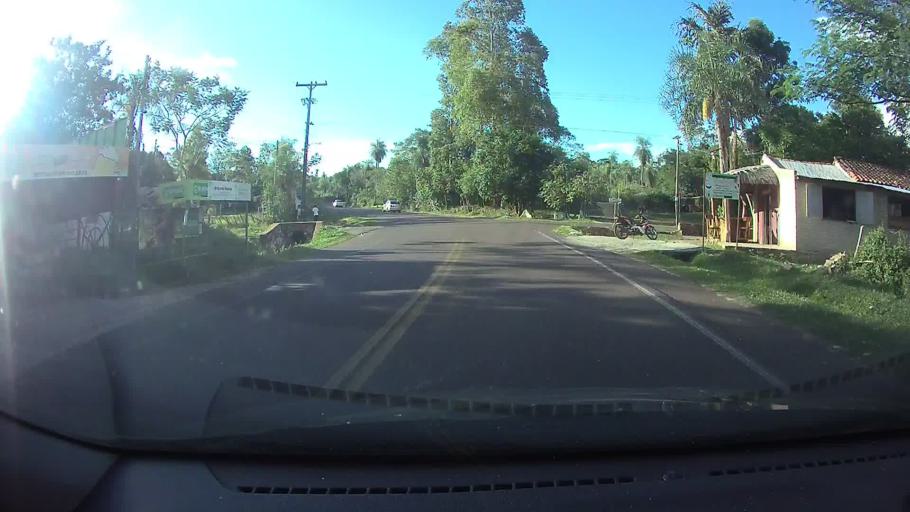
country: PY
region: Cordillera
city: Altos
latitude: -25.1872
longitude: -57.2252
